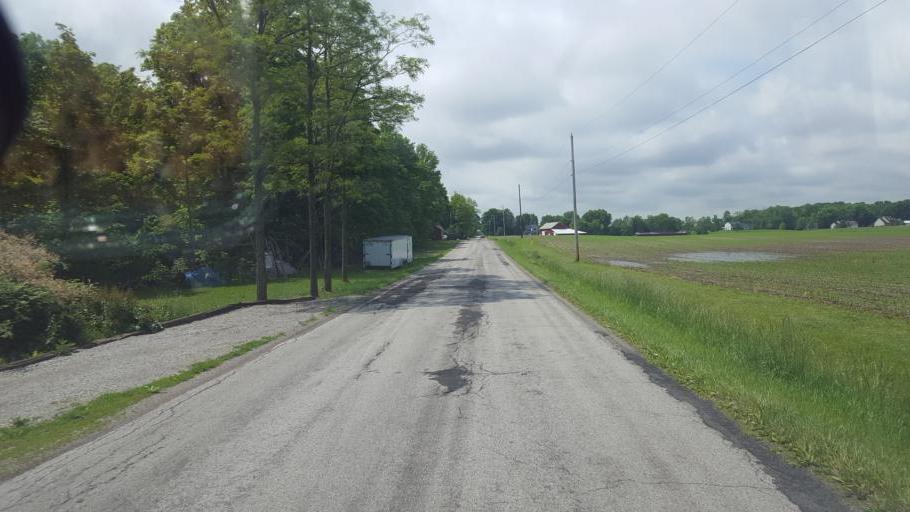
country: US
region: Ohio
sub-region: Delaware County
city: Ashley
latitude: 40.3999
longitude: -82.8726
